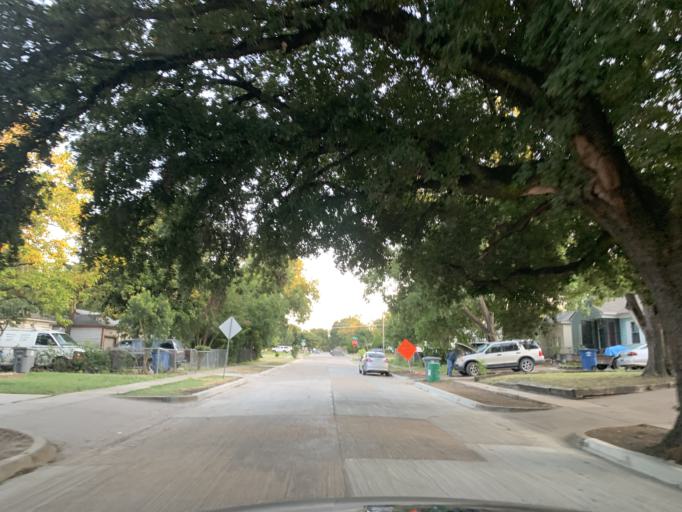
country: US
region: Texas
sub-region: Dallas County
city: Dallas
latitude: 32.7070
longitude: -96.8109
